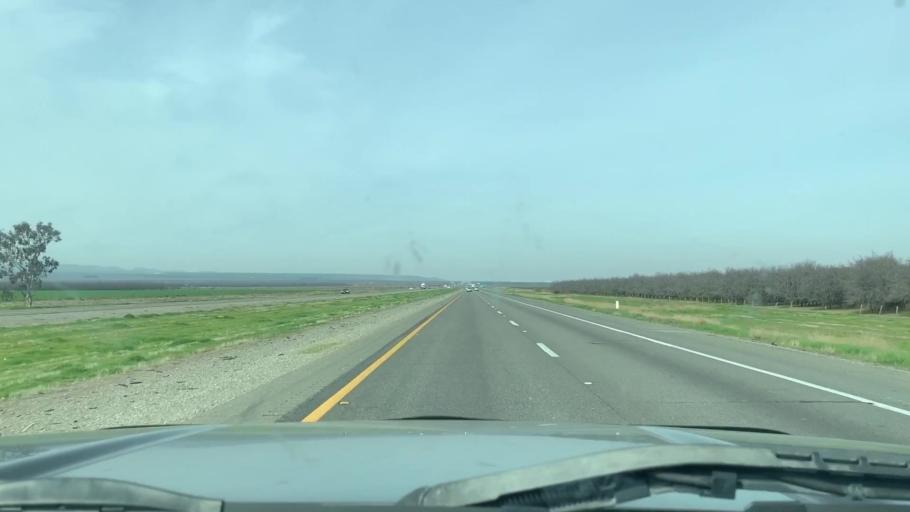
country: US
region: California
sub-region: Merced County
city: South Dos Palos
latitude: 36.7957
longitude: -120.7362
